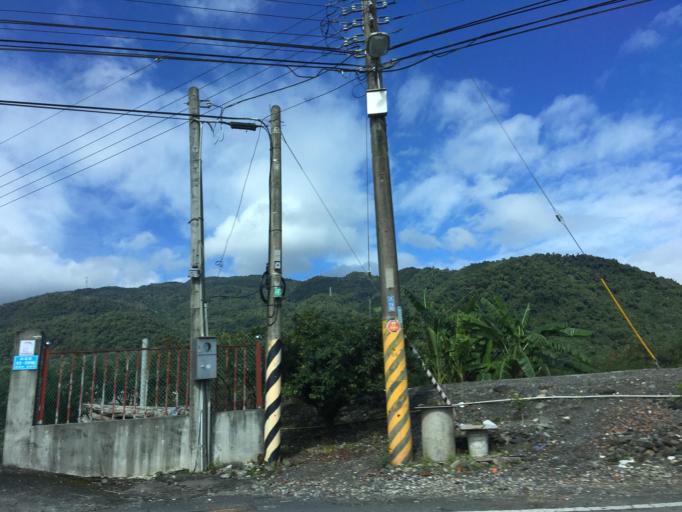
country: TW
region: Taiwan
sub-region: Yilan
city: Yilan
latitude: 24.8217
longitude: 121.7580
